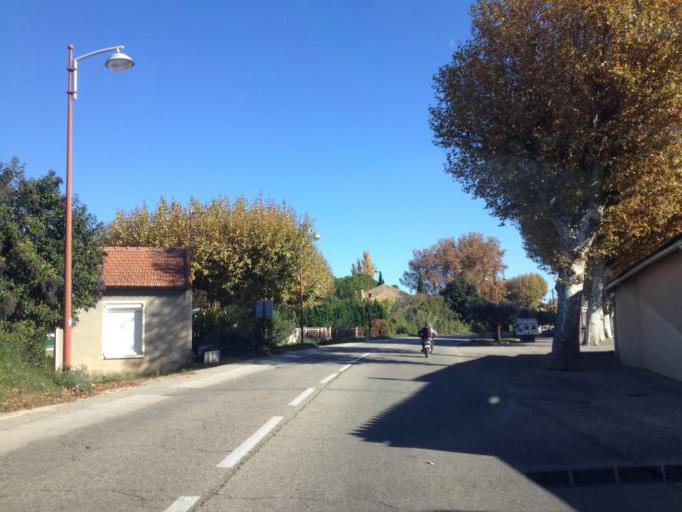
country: FR
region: Provence-Alpes-Cote d'Azur
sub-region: Departement du Vaucluse
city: Jonquieres
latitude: 44.1152
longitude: 4.9042
